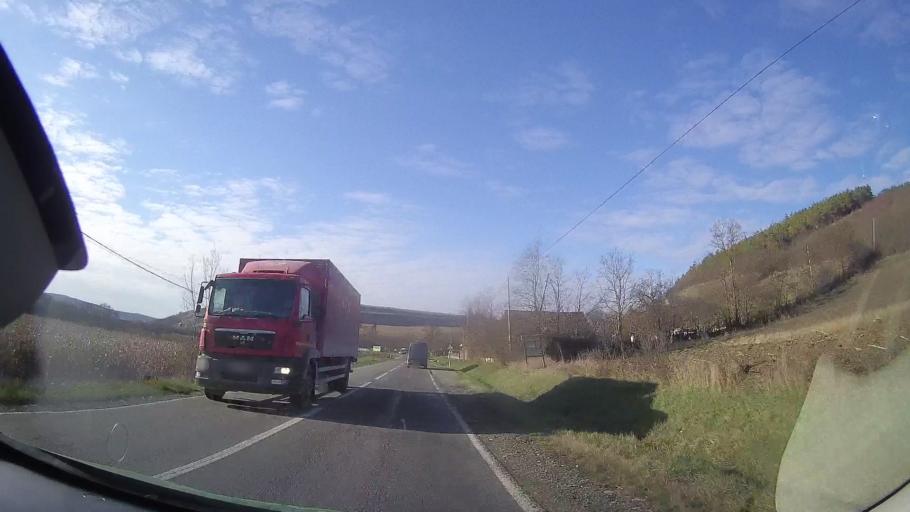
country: RO
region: Cluj
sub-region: Comuna Caianu
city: Caianu
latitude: 46.8017
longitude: 23.9335
